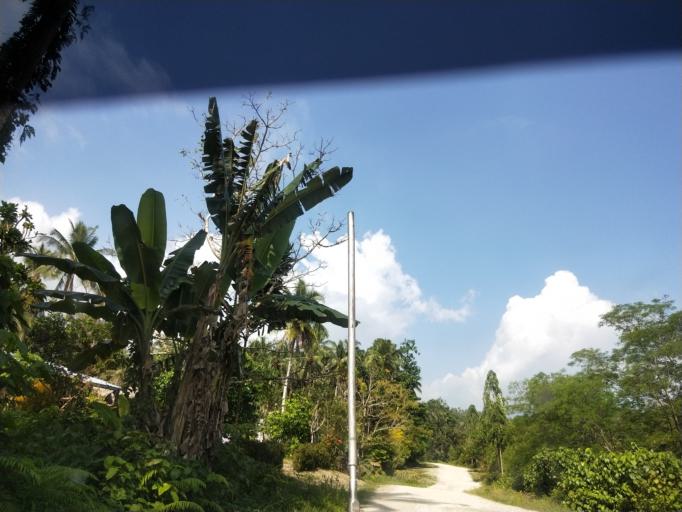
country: SB
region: Malaita
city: Auki
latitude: -8.4809
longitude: 160.6752
